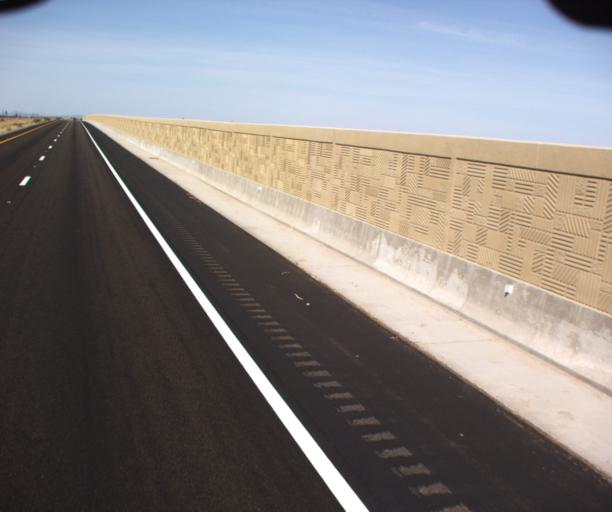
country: US
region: Arizona
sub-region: Yuma County
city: Somerton
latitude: 32.5494
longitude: -114.5620
